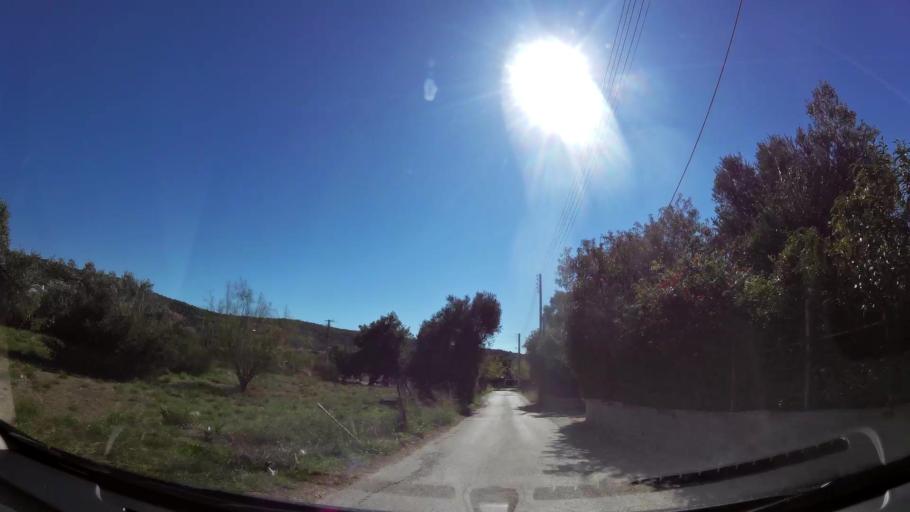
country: GR
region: Attica
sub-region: Nomarchia Anatolikis Attikis
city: Vari
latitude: 37.8348
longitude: 23.8203
